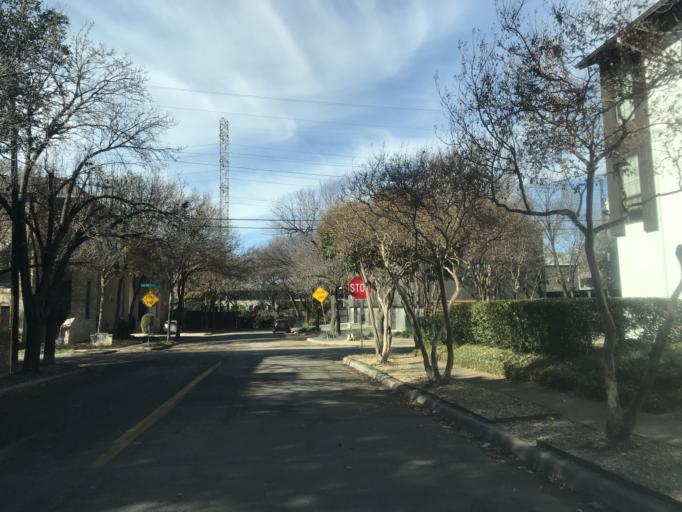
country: US
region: Texas
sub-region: Dallas County
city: Highland Park
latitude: 32.8207
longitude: -96.7927
